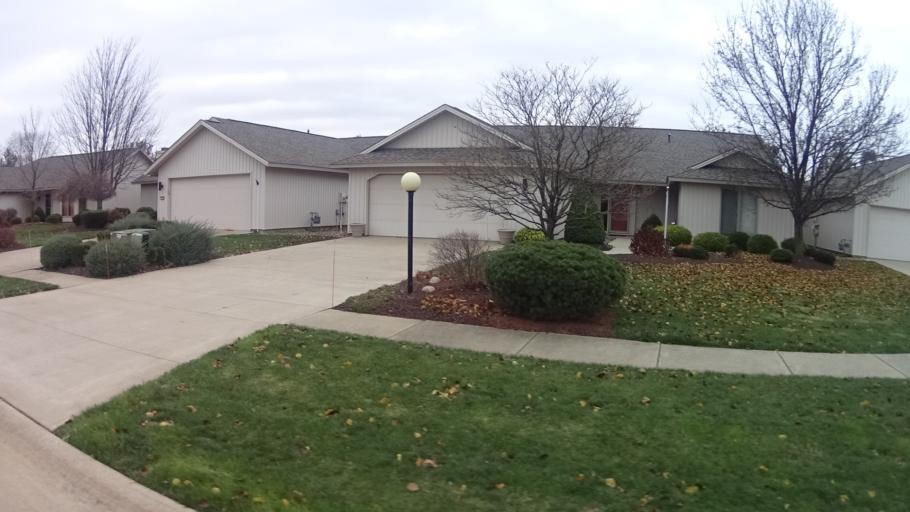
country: US
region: Ohio
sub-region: Lorain County
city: North Ridgeville
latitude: 41.3590
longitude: -81.9874
